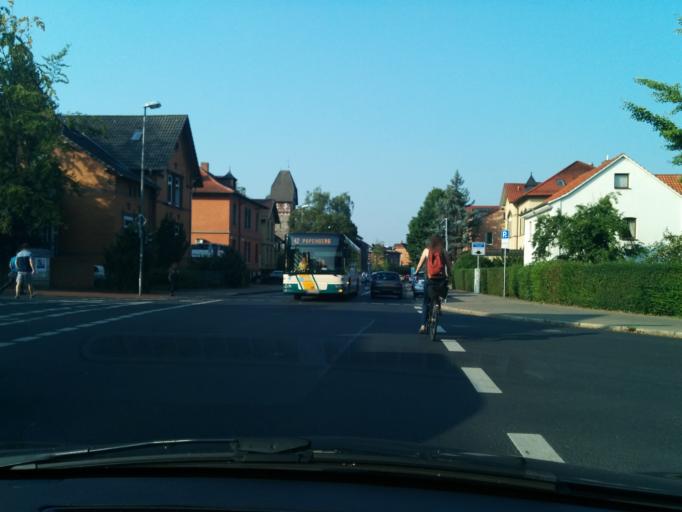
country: DE
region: Lower Saxony
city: Goettingen
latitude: 51.5407
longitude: 9.9447
